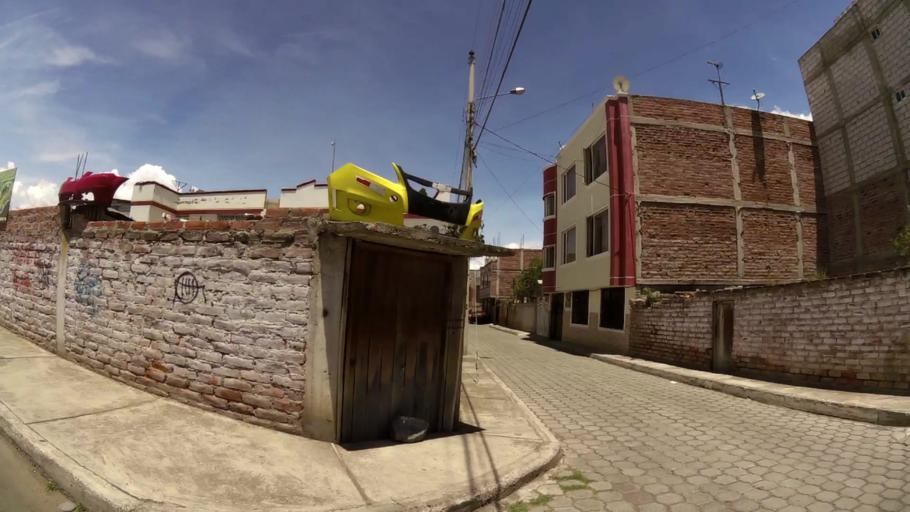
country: EC
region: Chimborazo
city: Riobamba
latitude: -1.6872
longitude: -78.6367
